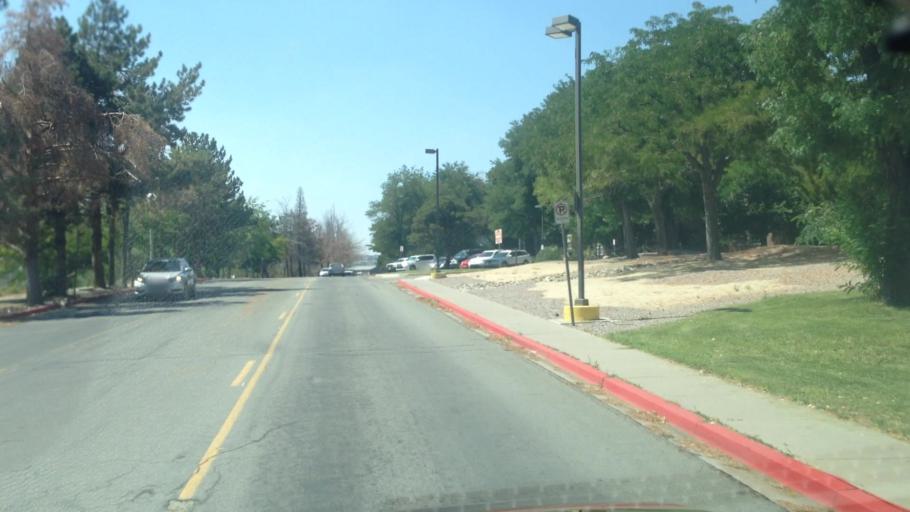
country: US
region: Nevada
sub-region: Washoe County
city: Sparks
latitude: 39.5283
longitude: -119.7774
